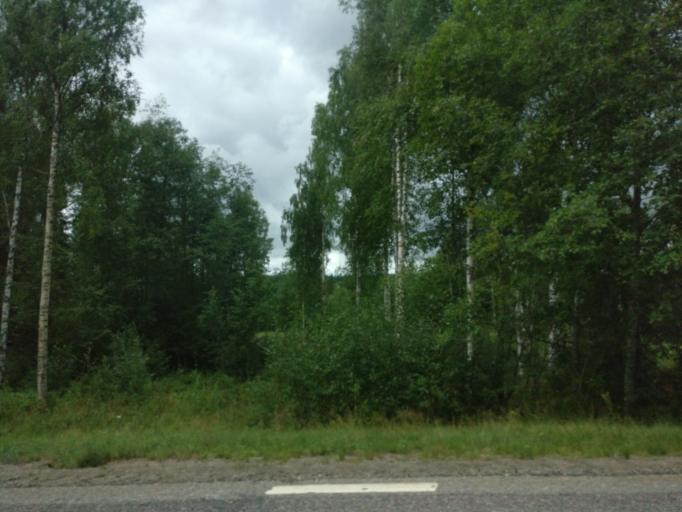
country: SE
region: Vaermland
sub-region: Torsby Kommun
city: Torsby
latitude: 60.7678
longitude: 12.7582
